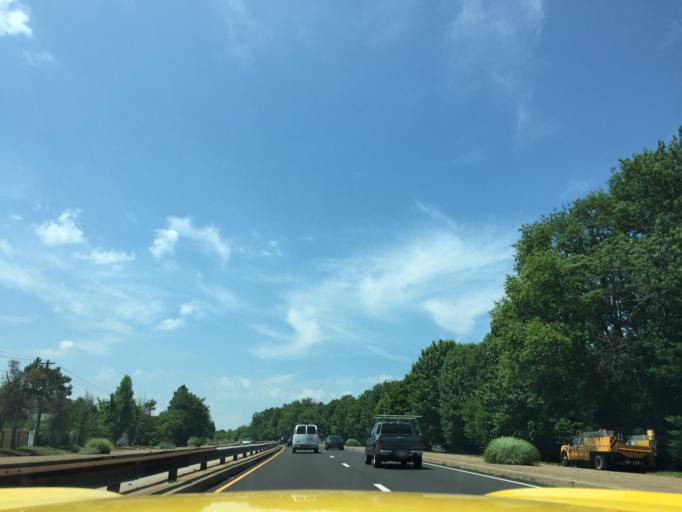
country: US
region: Pennsylvania
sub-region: Bucks County
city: Langhorne
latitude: 40.1643
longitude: -74.9303
